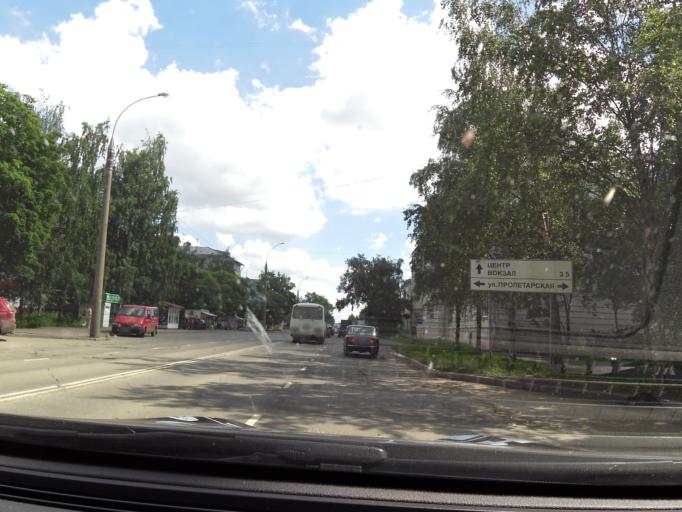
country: RU
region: Vologda
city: Vologda
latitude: 59.2263
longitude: 39.8648
